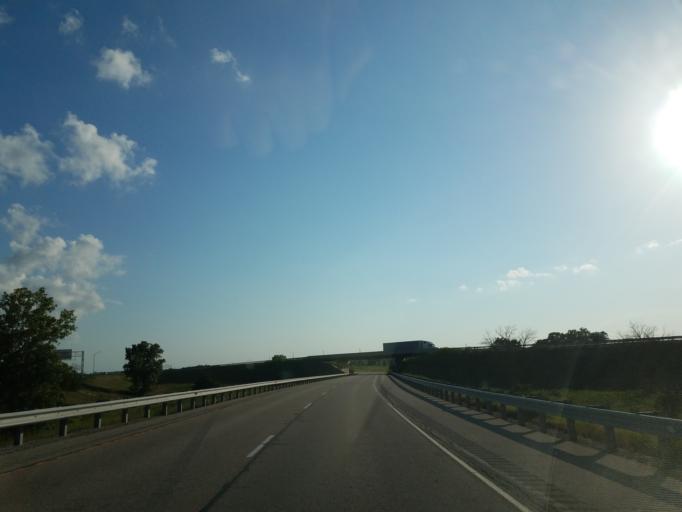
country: US
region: Illinois
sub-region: McLean County
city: Bloomington
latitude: 40.4398
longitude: -89.0215
